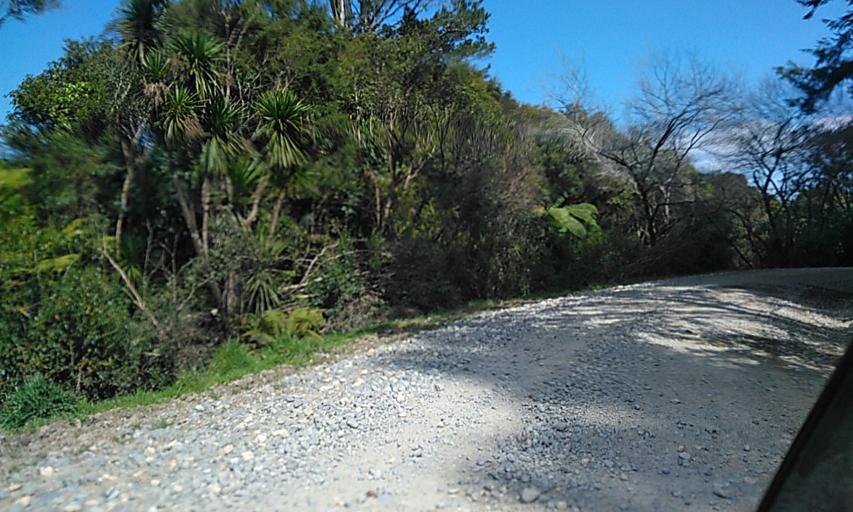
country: NZ
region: Gisborne
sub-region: Gisborne District
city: Gisborne
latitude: -38.2162
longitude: 178.0695
